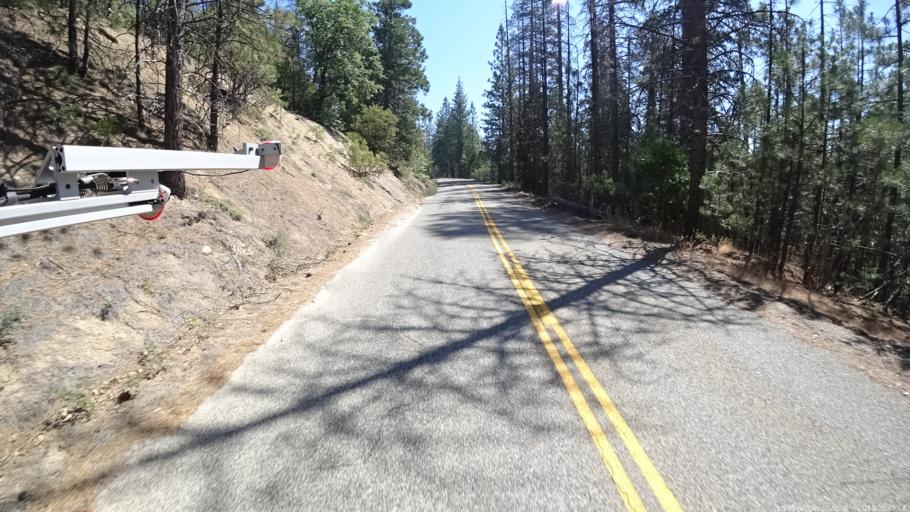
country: US
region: California
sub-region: Madera County
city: Oakhurst
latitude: 37.4004
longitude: -119.3496
